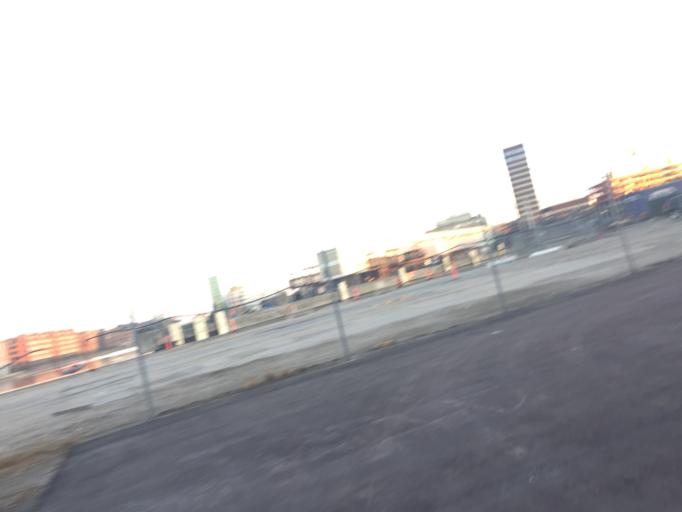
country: DK
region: Capital Region
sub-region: Kobenhavn
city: Christianshavn
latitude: 55.7039
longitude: 12.5974
